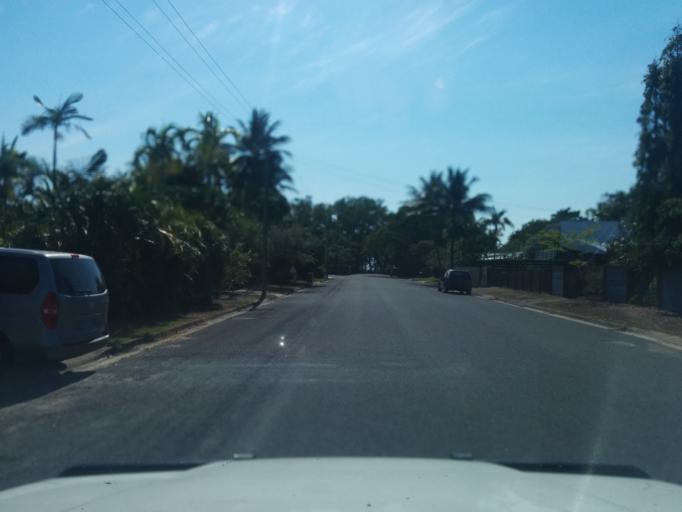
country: AU
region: Queensland
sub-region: Cairns
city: Yorkeys Knob
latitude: -16.8444
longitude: 145.7421
